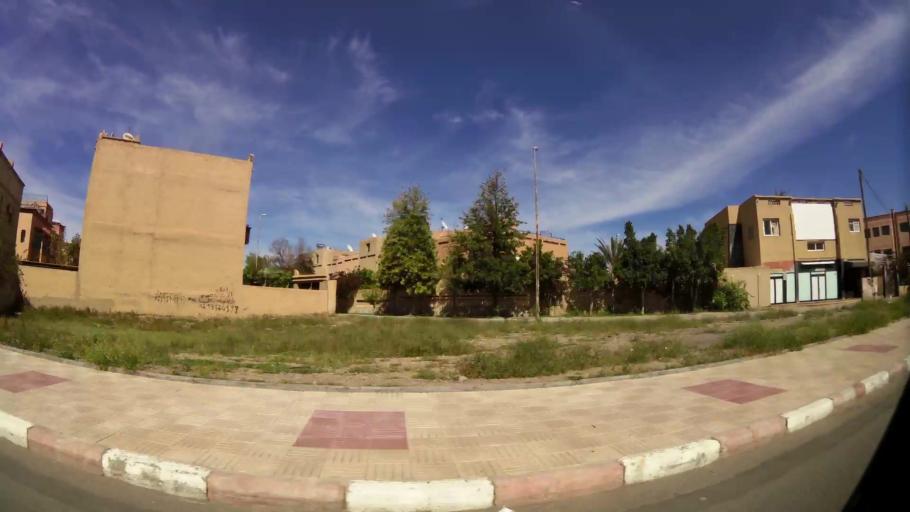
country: MA
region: Marrakech-Tensift-Al Haouz
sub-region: Marrakech
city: Marrakesh
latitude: 31.6791
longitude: -8.0008
